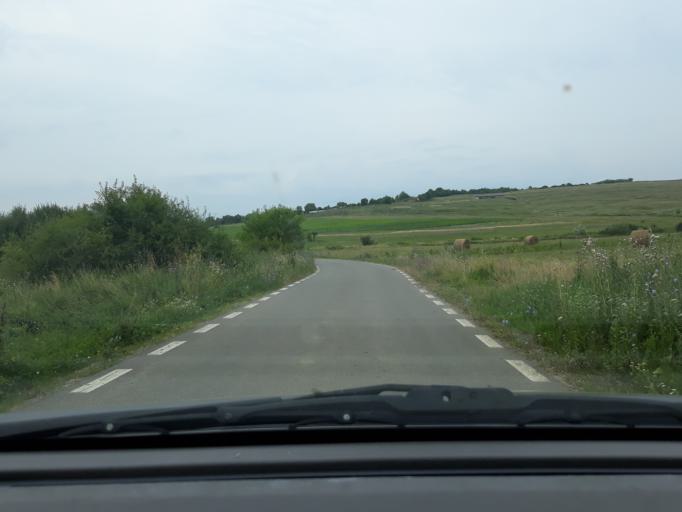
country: RO
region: Salaj
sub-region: Comuna Criseni
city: Criseni
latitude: 47.2686
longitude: 23.0680
